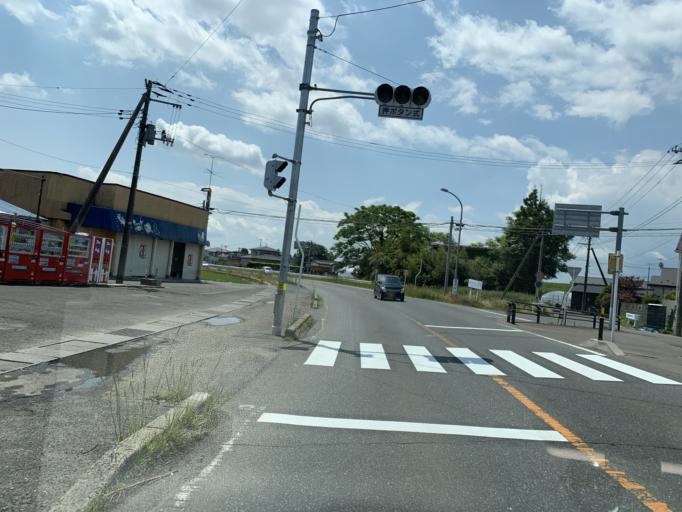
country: JP
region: Miyagi
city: Kogota
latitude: 38.5334
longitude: 141.0545
